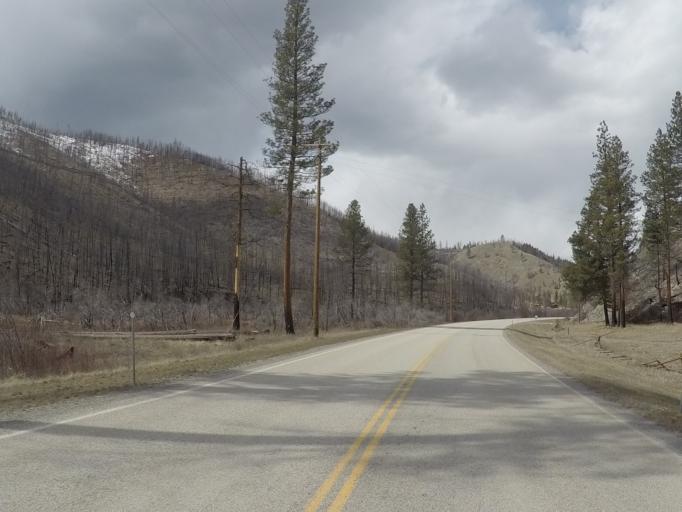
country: US
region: Montana
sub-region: Missoula County
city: Lolo
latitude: 46.7577
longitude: -114.3173
